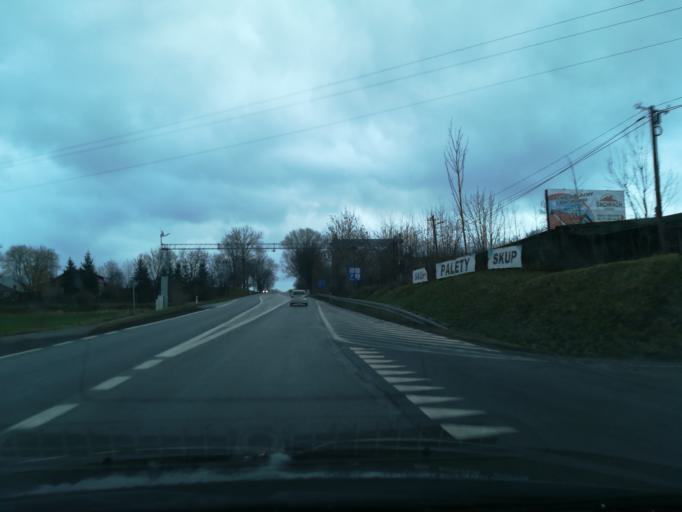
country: PL
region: Subcarpathian Voivodeship
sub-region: Powiat lancucki
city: Gluchow
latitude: 50.0811
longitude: 22.2736
